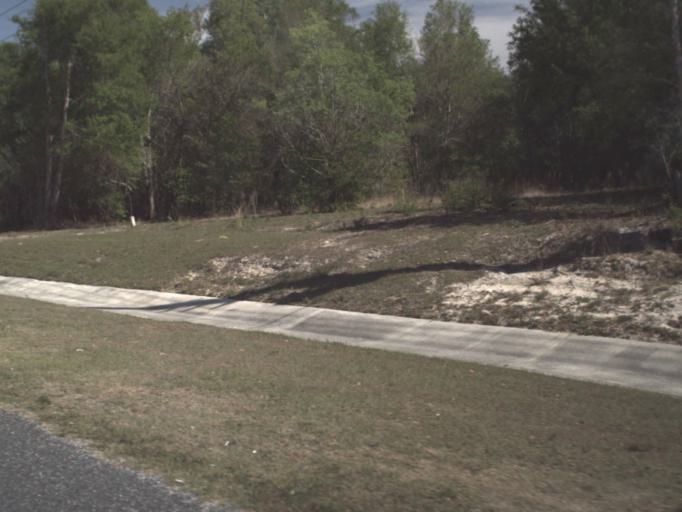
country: US
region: Florida
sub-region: Lake County
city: Lady Lake
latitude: 28.9018
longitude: -81.9133
